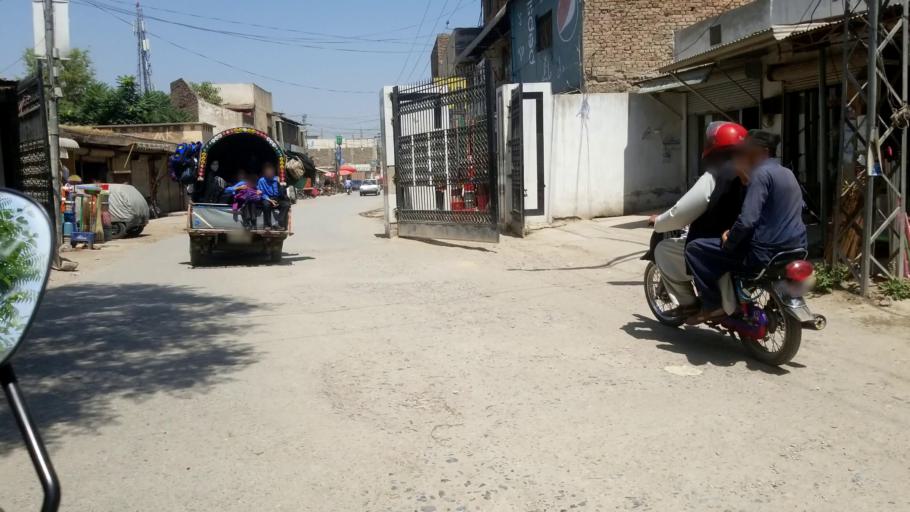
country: PK
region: Khyber Pakhtunkhwa
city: Peshawar
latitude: 34.0225
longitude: 71.4851
